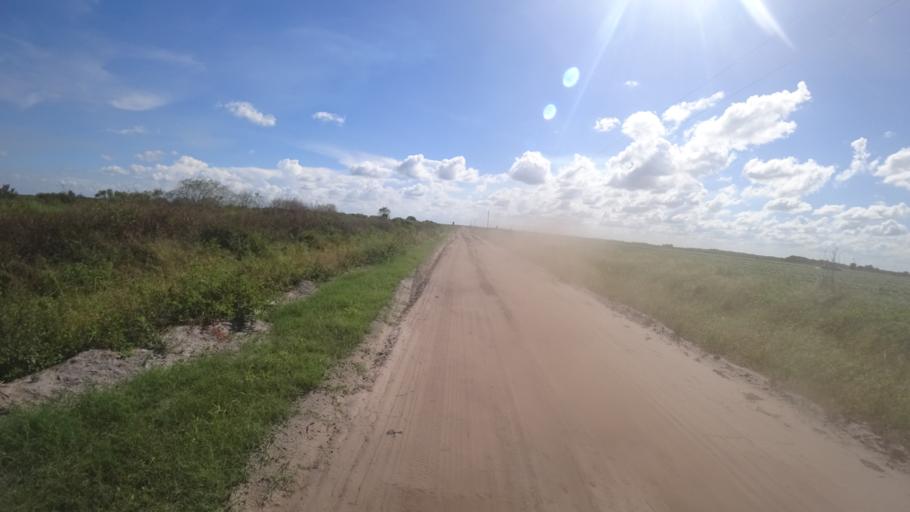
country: US
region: Florida
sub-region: DeSoto County
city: Arcadia
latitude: 27.3355
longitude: -82.0969
